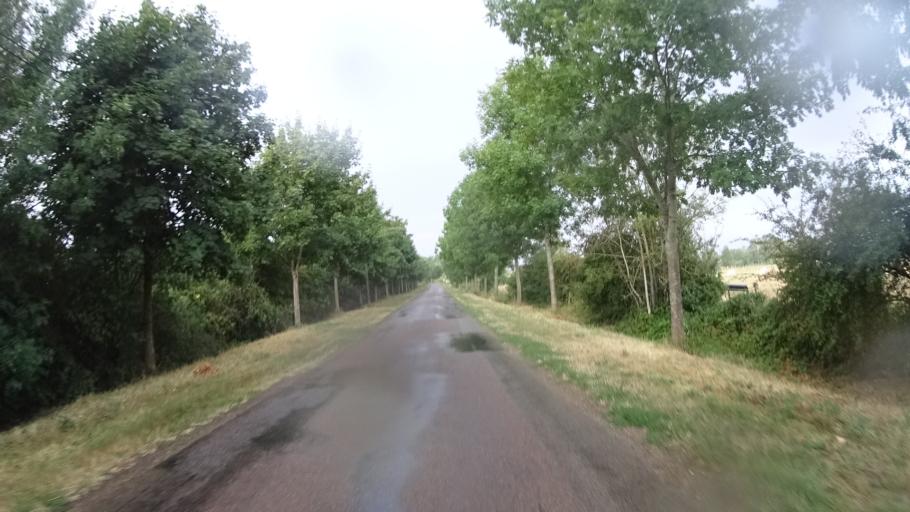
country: FR
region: Bourgogne
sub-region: Departement de Saone-et-Loire
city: Verdun-sur-le-Doubs
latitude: 46.9627
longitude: 5.0217
